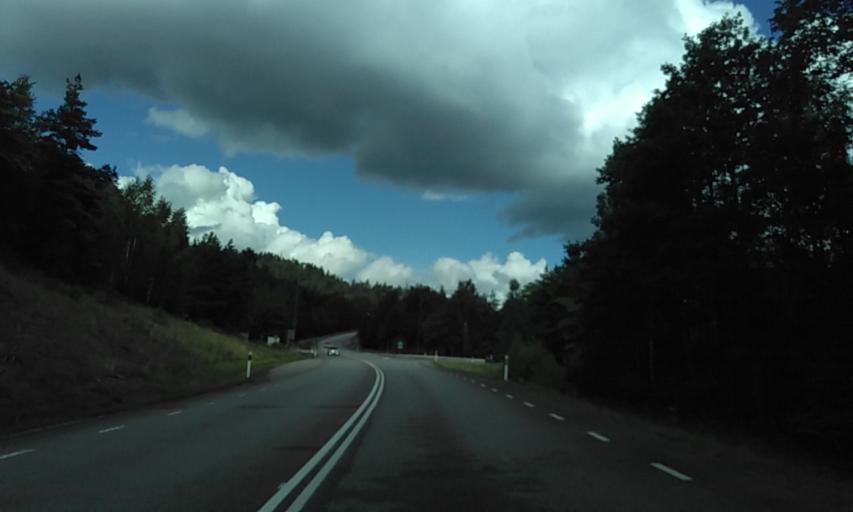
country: SE
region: Vaestra Goetaland
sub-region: Alingsas Kommun
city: Alingsas
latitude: 57.9743
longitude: 12.4327
